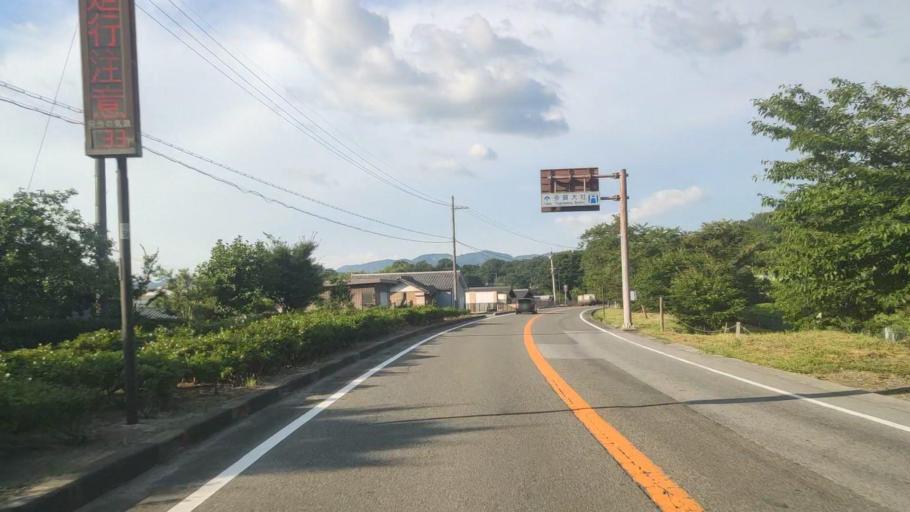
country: JP
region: Shiga Prefecture
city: Hikone
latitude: 35.2125
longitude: 136.2819
